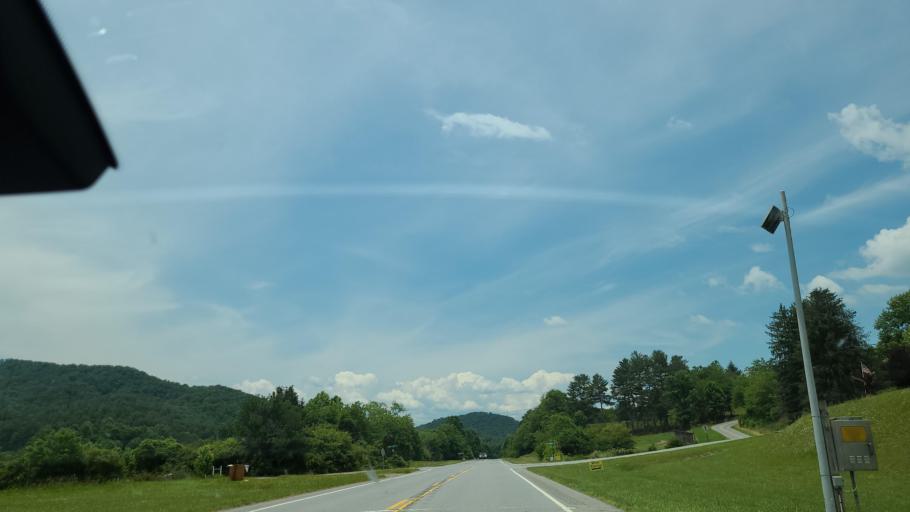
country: US
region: Georgia
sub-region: Towns County
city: Hiawassee
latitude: 35.0247
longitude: -83.6815
